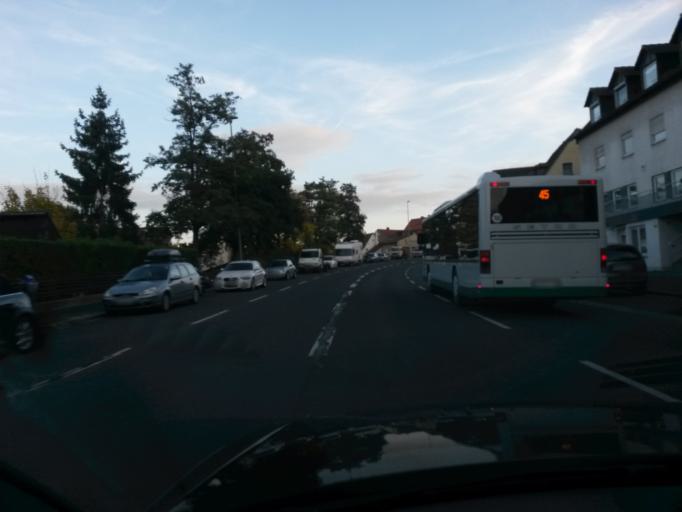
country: DE
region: Bavaria
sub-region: Regierungsbezirk Unterfranken
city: Wuerzburg
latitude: 49.8195
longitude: 9.9629
